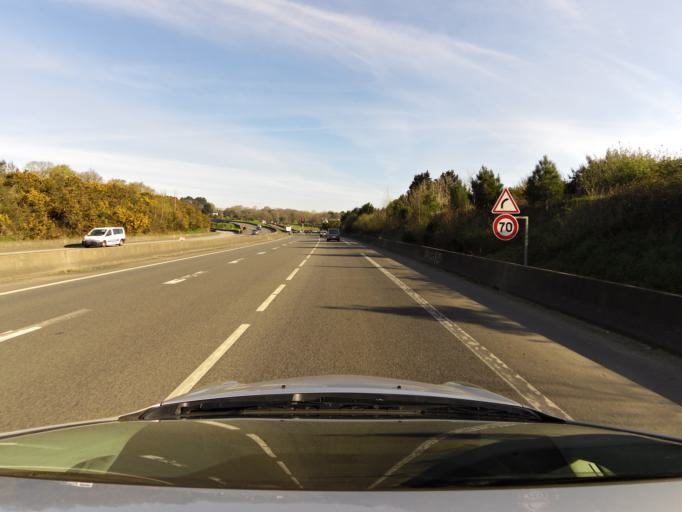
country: FR
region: Brittany
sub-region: Departement du Morbihan
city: Lorient
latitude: 47.7681
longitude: -3.3782
